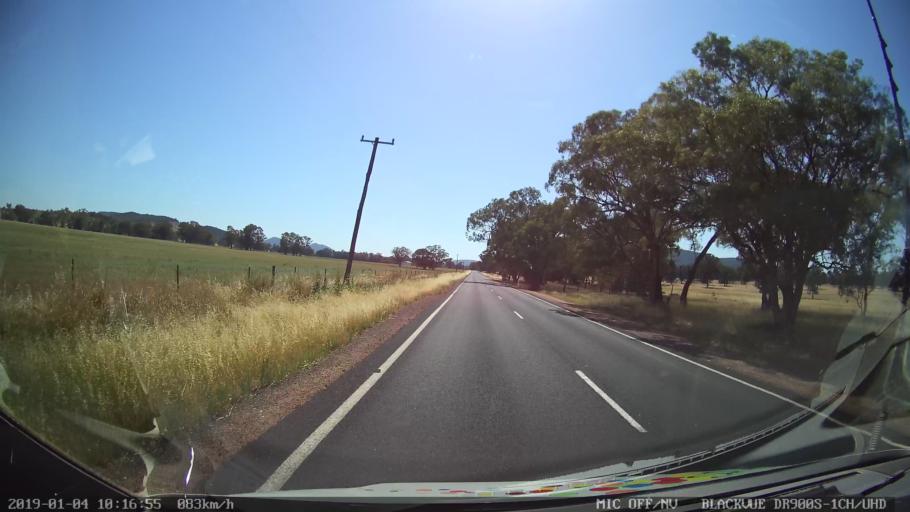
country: AU
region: New South Wales
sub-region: Cabonne
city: Canowindra
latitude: -33.3847
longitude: 148.4437
